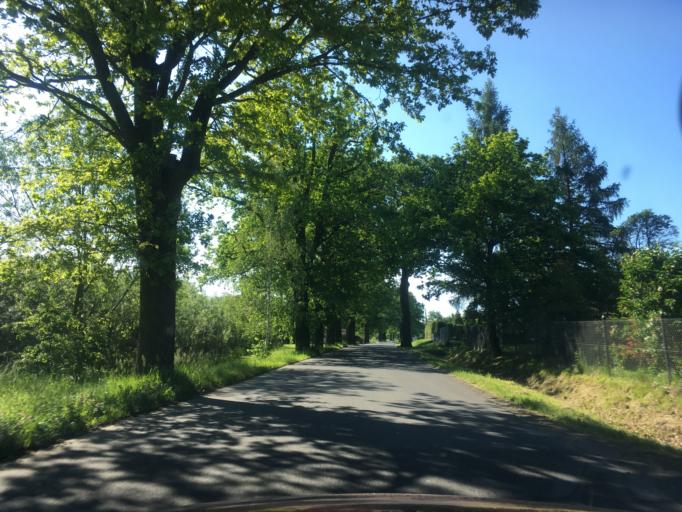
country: PL
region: Lower Silesian Voivodeship
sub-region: Powiat zgorzelecki
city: Sulikow
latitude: 51.0893
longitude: 15.0524
